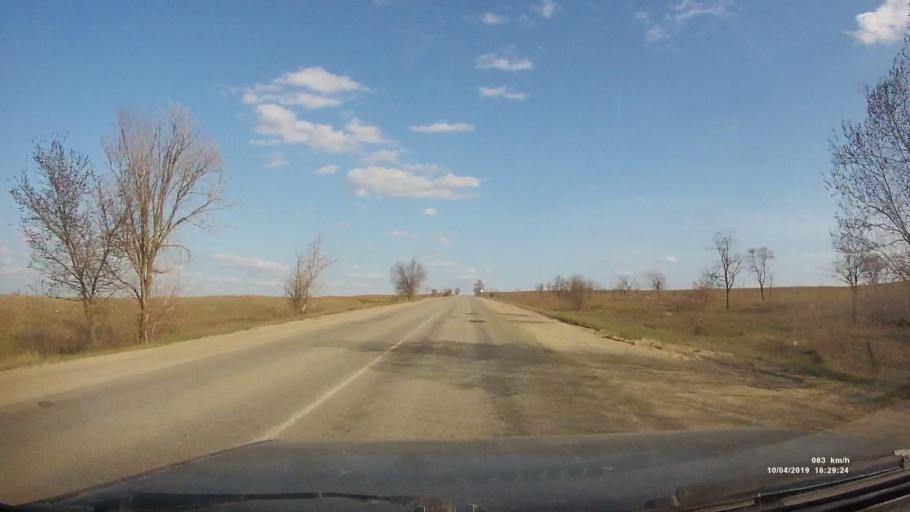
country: RU
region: Rostov
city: Staraya Stanitsa
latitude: 48.2686
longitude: 40.3548
